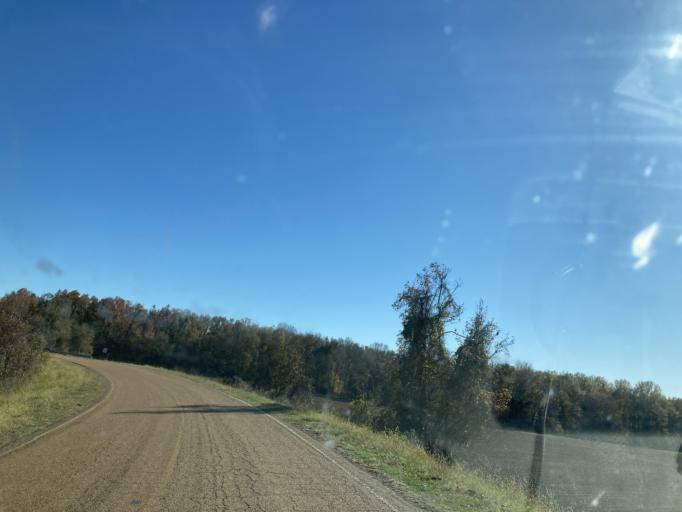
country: US
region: Mississippi
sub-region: Yazoo County
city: Yazoo City
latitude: 32.7764
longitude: -90.6376
